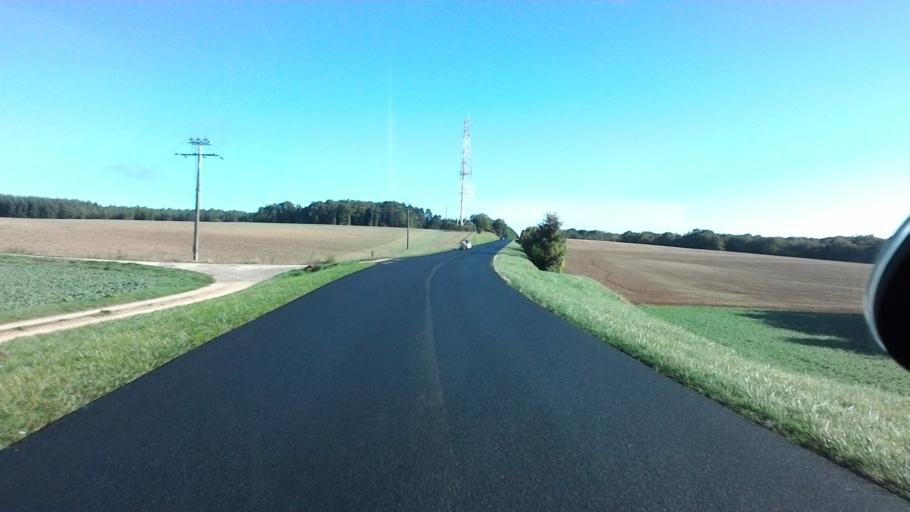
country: FR
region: Bourgogne
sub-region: Departement de la Cote-d'Or
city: Montbard
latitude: 47.6408
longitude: 4.3610
